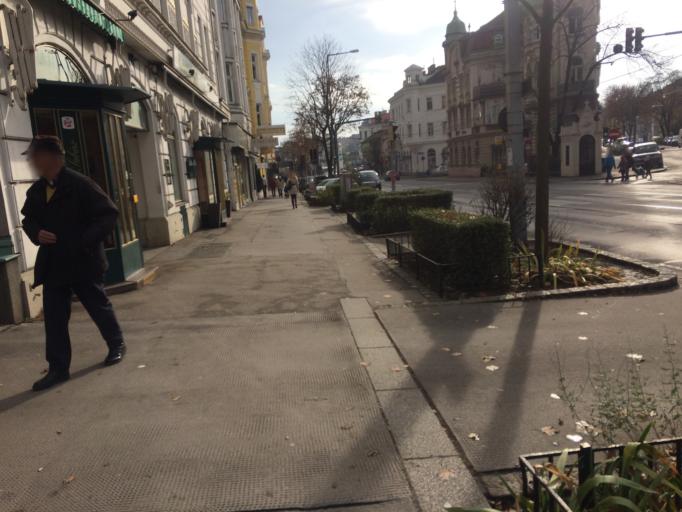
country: AT
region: Vienna
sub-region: Wien Stadt
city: Vienna
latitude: 48.2332
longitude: 16.3280
